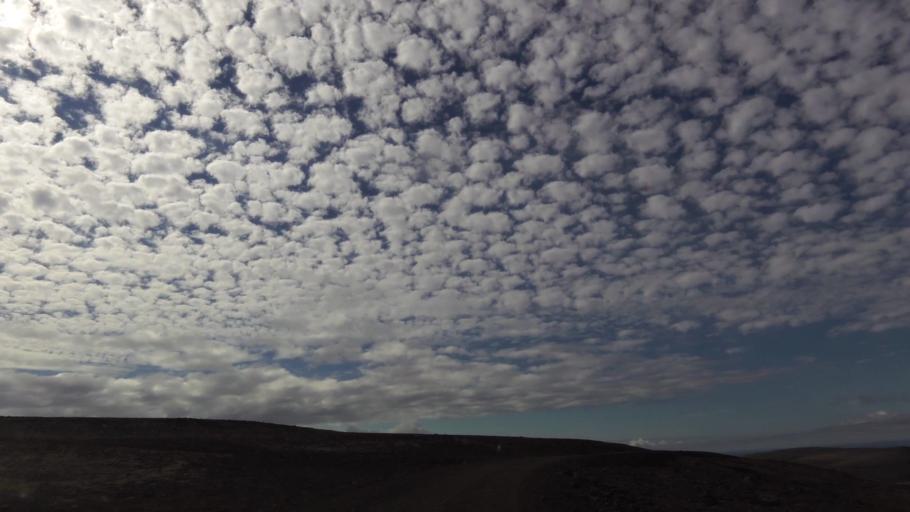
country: IS
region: West
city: Olafsvik
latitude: 65.6202
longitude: -24.2760
